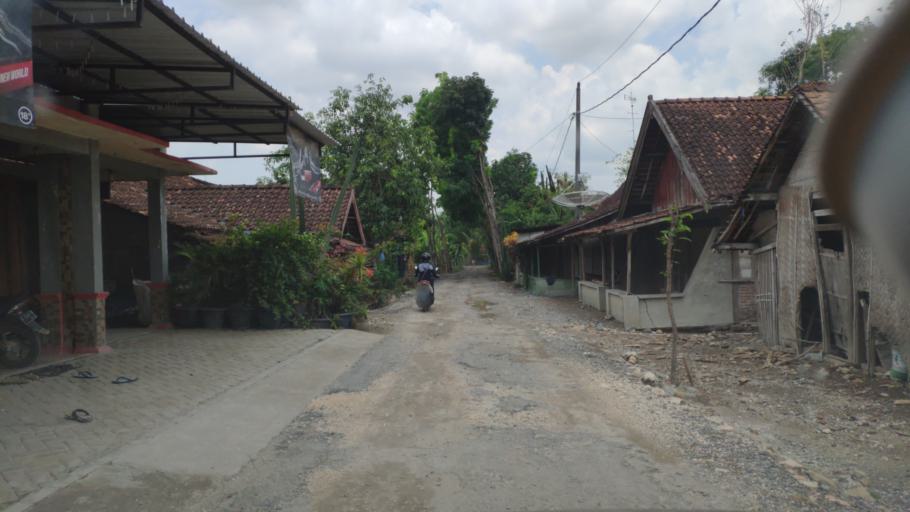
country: ID
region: Central Java
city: Gumiring
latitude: -7.0403
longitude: 111.3895
